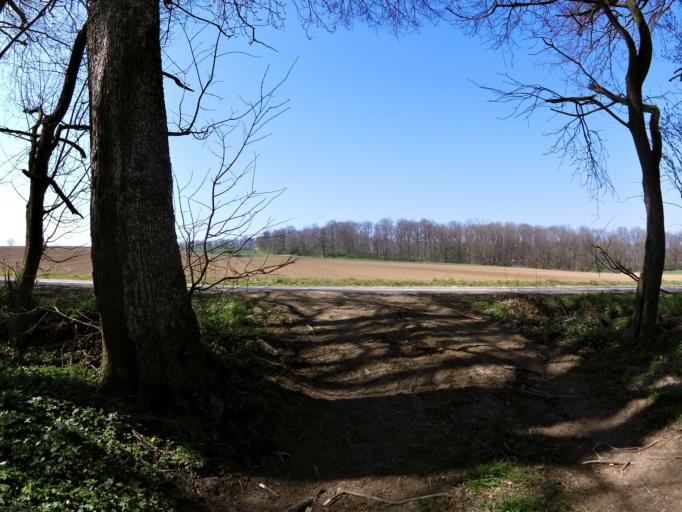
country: DE
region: Bavaria
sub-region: Regierungsbezirk Unterfranken
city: Biebelried
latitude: 49.7725
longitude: 10.0865
